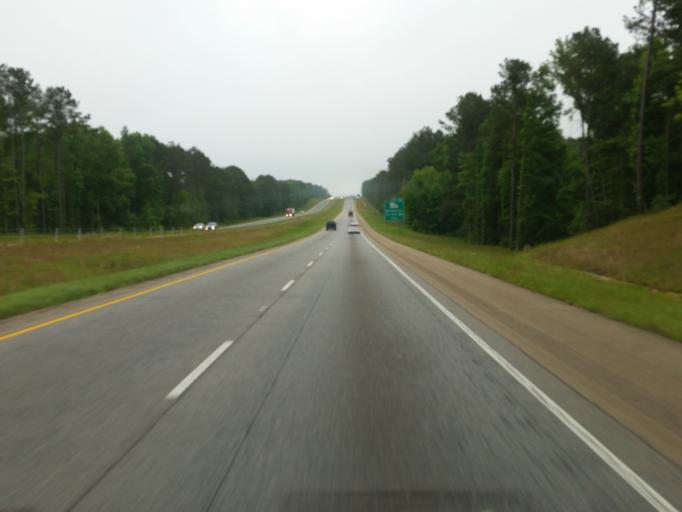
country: US
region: Louisiana
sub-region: Webster Parish
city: Minden
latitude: 32.5752
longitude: -93.2232
